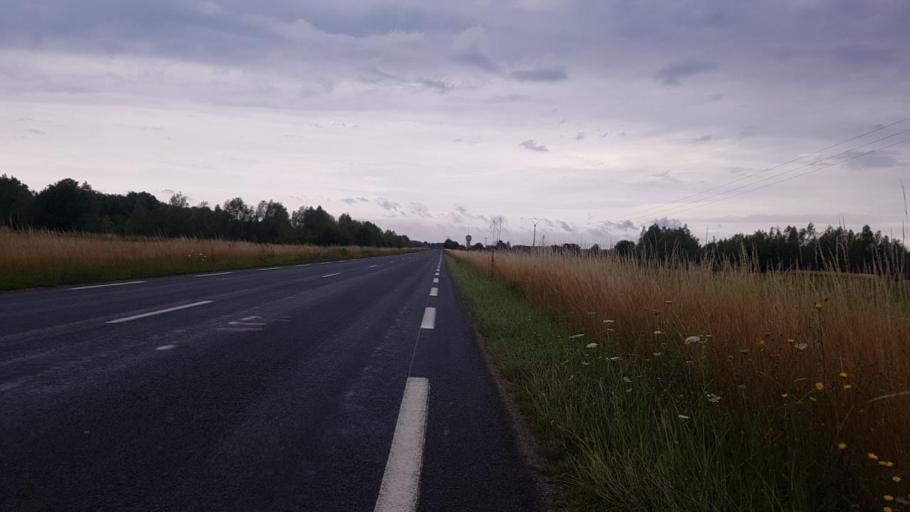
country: FR
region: Champagne-Ardenne
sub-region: Departement de la Marne
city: Vitry-le-Francois
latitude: 48.7451
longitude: 4.6844
